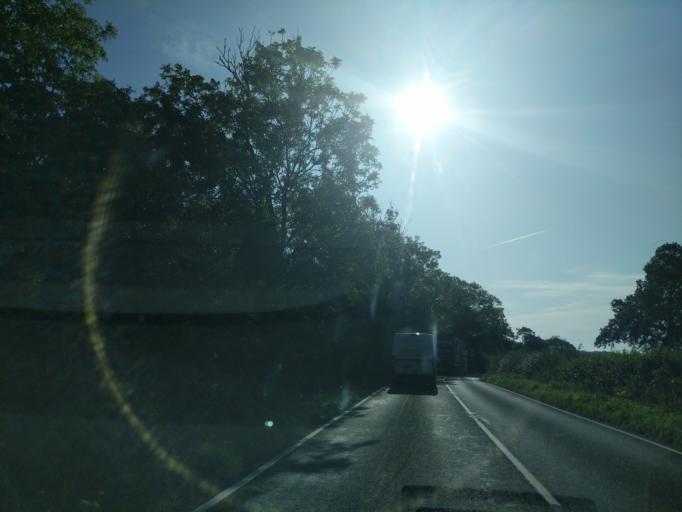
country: GB
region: England
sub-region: District of Rutland
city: Pickworth
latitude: 52.8067
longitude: -0.4856
